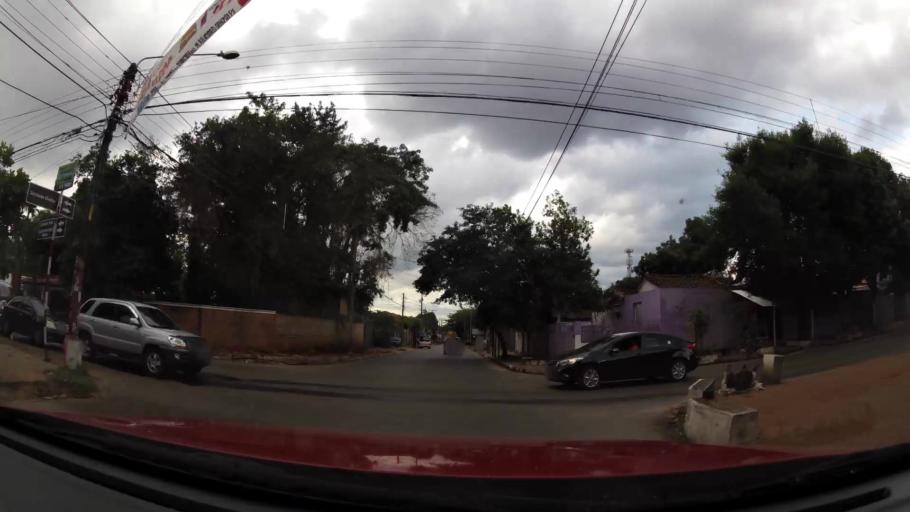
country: PY
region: Central
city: Fernando de la Mora
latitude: -25.3305
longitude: -57.5638
